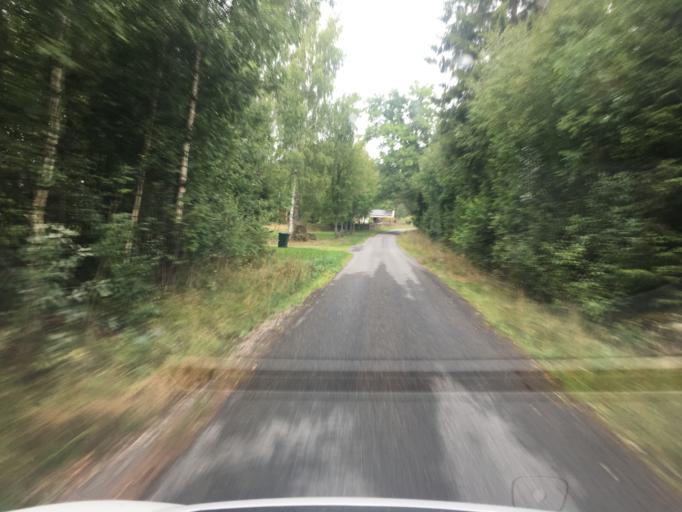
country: SE
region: Kronoberg
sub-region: Ljungby Kommun
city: Lagan
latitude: 56.9533
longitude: 14.0373
